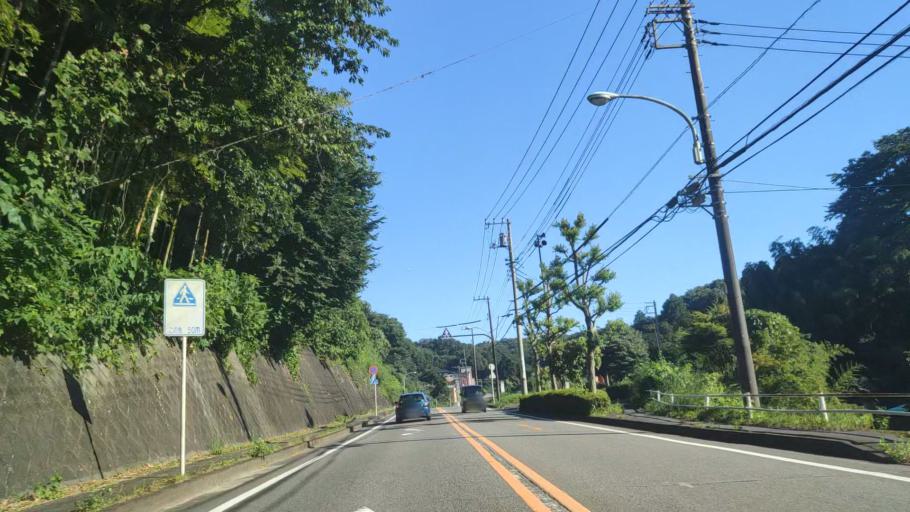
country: JP
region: Tokyo
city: Hachioji
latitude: 35.6199
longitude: 139.3145
